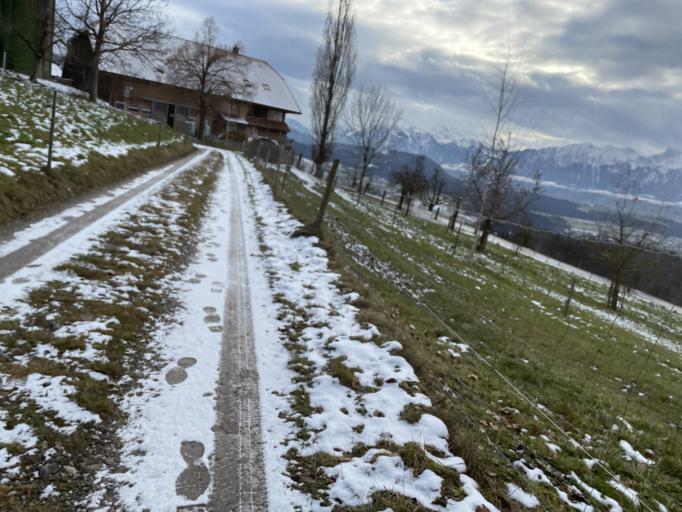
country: CH
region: Lucerne
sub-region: Entlebuch District
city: Oberdiessbach
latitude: 46.8434
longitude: 7.6056
